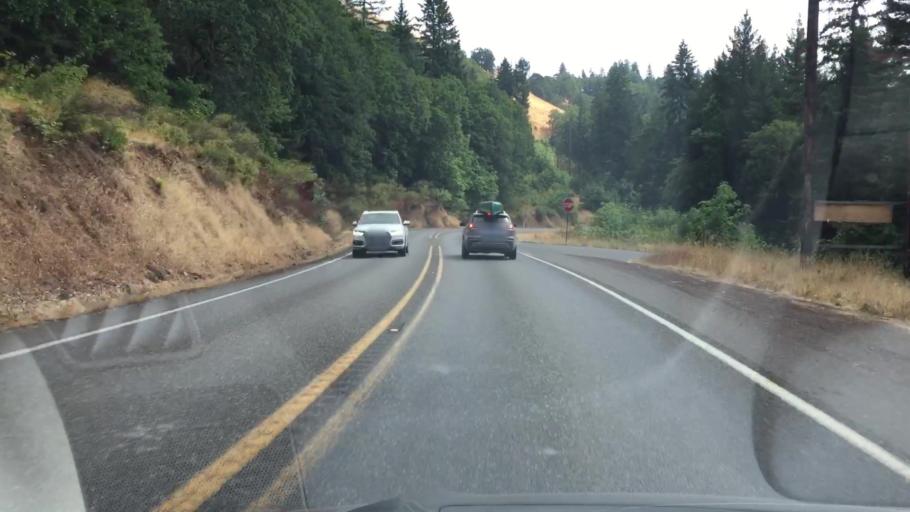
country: US
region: Washington
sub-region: Klickitat County
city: White Salmon
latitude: 45.7526
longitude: -121.5177
